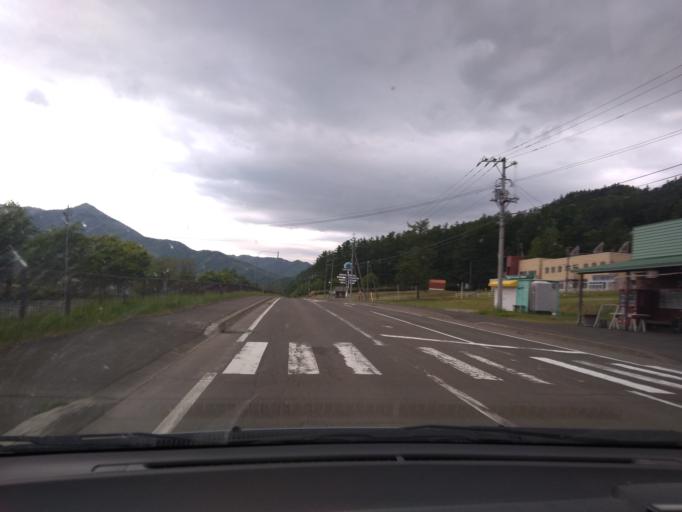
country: JP
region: Hokkaido
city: Shimo-furano
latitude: 43.1595
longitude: 142.4908
